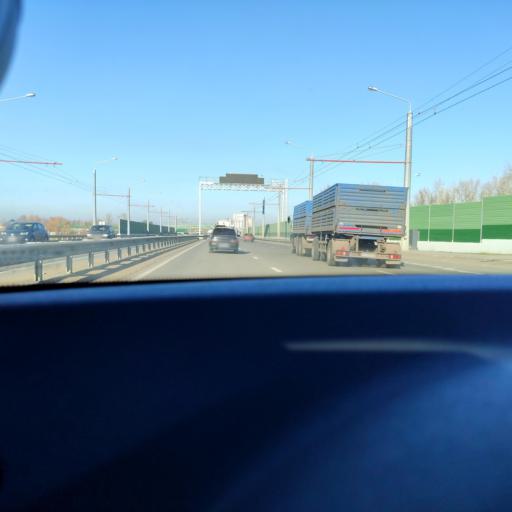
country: RU
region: Samara
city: Samara
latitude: 53.1609
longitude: 50.0895
